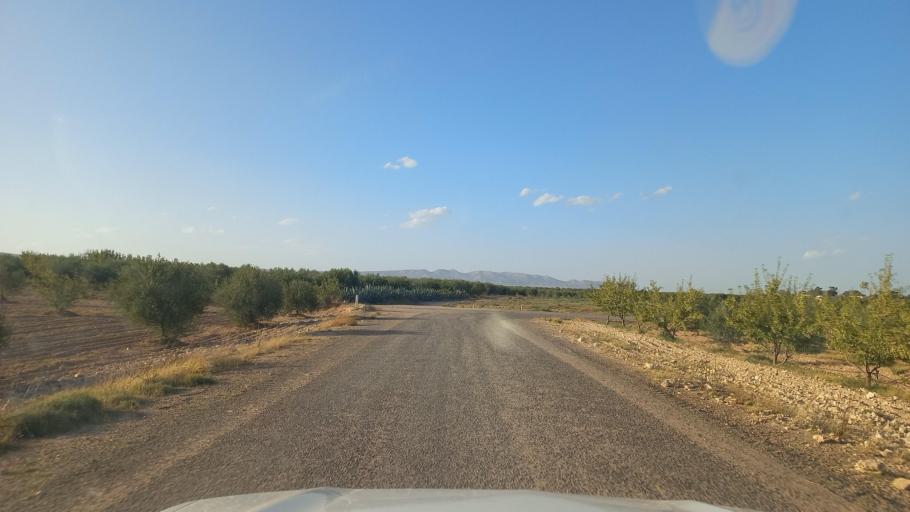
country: TN
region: Al Qasrayn
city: Kasserine
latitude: 35.2861
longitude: 9.0270
